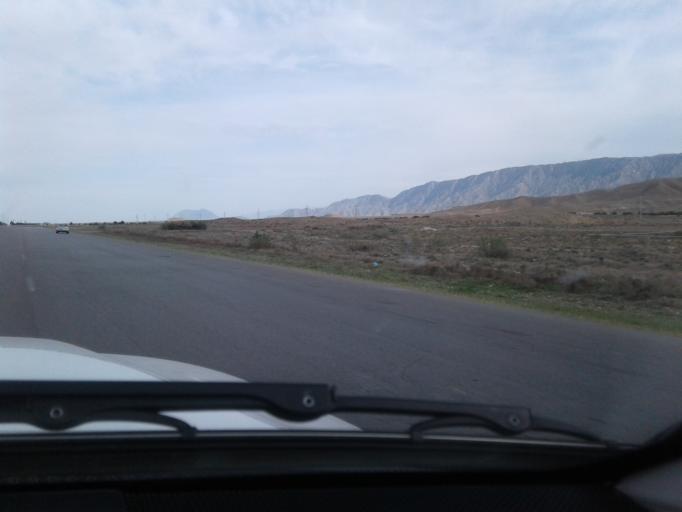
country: TM
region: Ahal
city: Baharly
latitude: 38.2382
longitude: 57.7715
